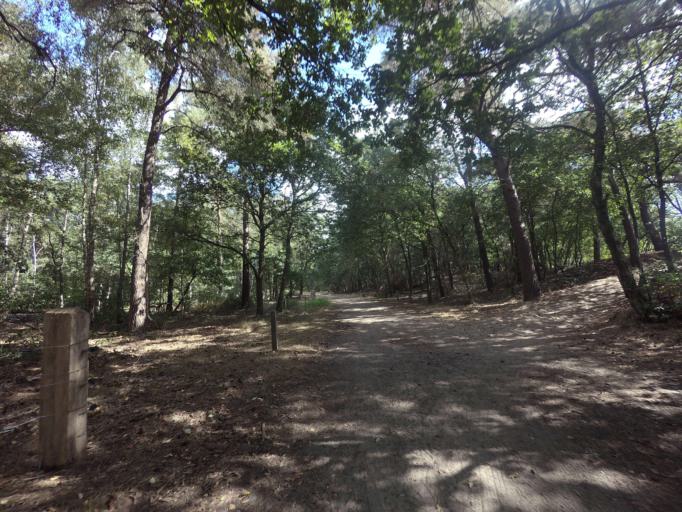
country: NL
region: North Brabant
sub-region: Gemeente Landerd
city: Schaijk
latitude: 51.7535
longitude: 5.6075
